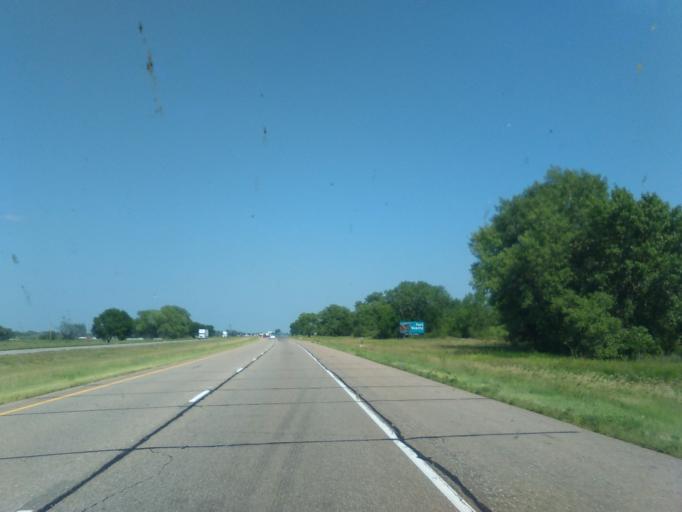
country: US
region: Nebraska
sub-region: Buffalo County
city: Kearney
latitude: 40.6700
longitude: -99.1470
